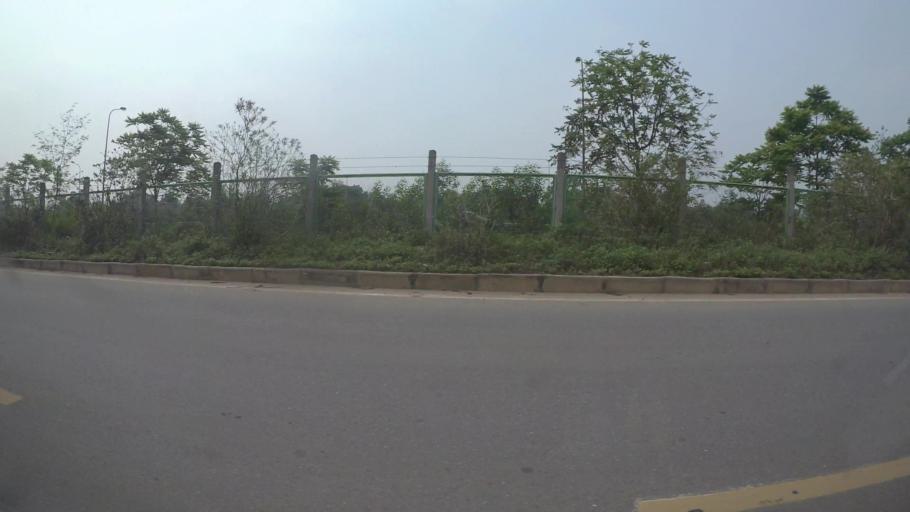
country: VN
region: Ha Noi
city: Lien Quan
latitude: 20.9909
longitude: 105.5431
